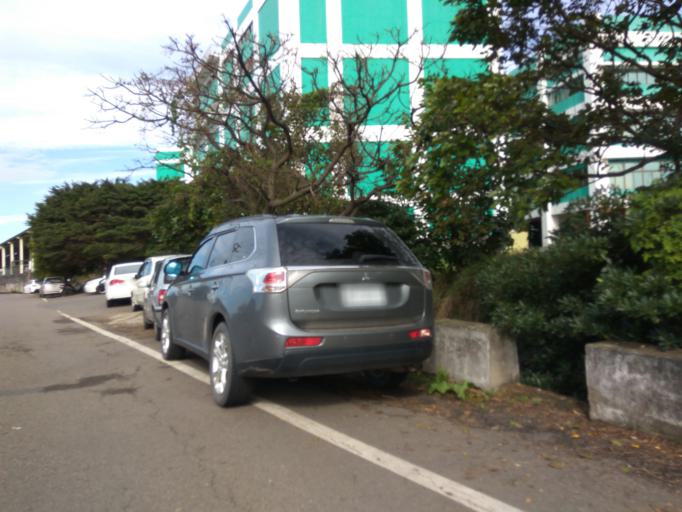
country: TW
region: Taiwan
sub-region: Hsinchu
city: Zhubei
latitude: 24.9917
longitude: 121.0998
